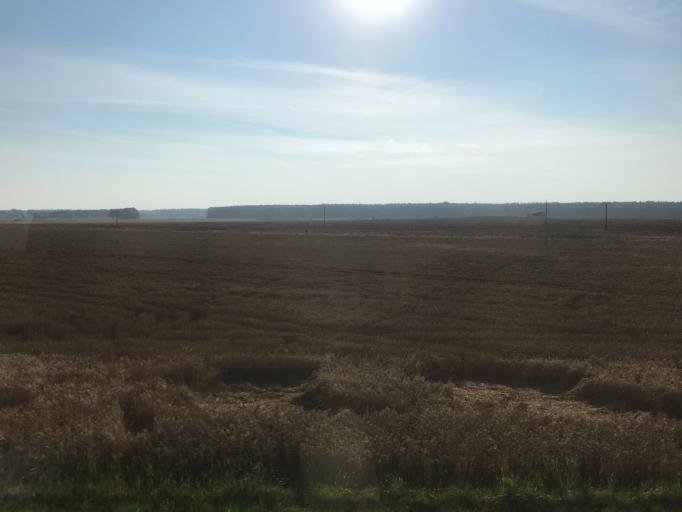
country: CZ
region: Jihocesky
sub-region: Okres Jindrichuv Hradec
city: Lomnice nad Luznici
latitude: 49.0798
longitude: 14.7256
